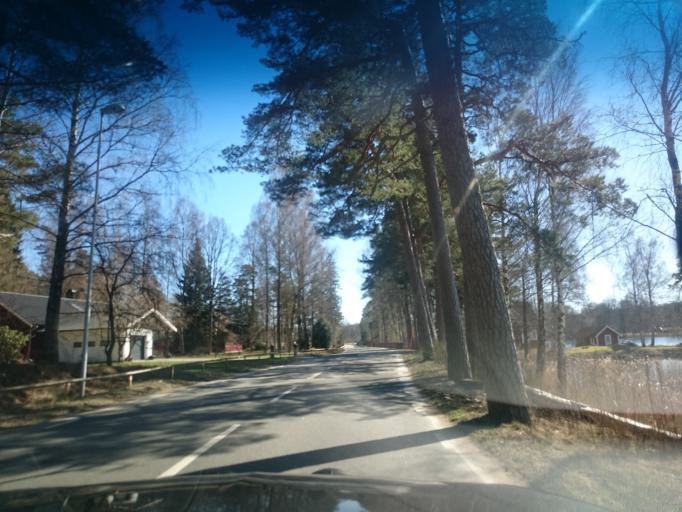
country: SE
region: Kronoberg
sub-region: Vaxjo Kommun
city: Braas
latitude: 57.2005
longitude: 14.9575
